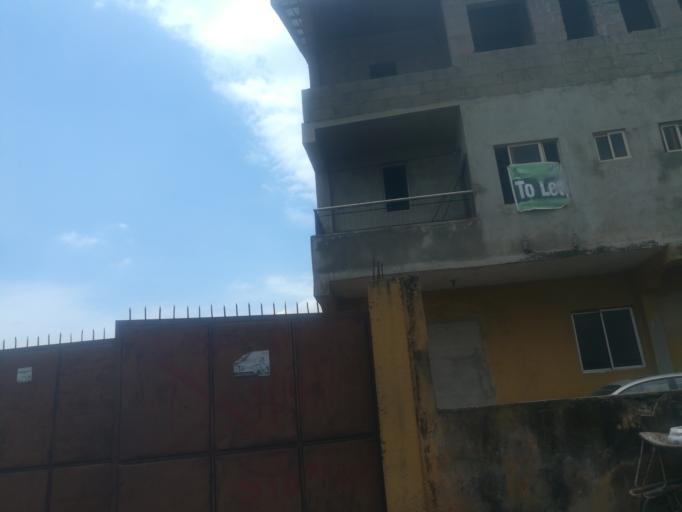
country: NG
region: Lagos
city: Somolu
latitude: 6.5512
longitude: 3.3929
